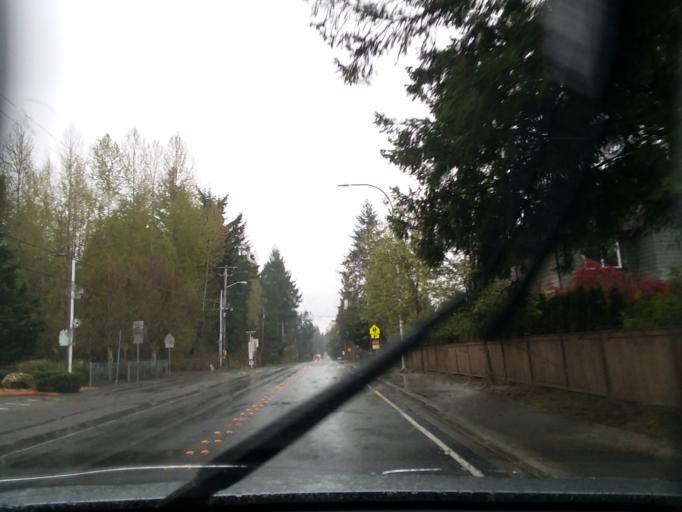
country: US
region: Washington
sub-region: King County
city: Fairwood
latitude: 47.4817
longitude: -122.1483
